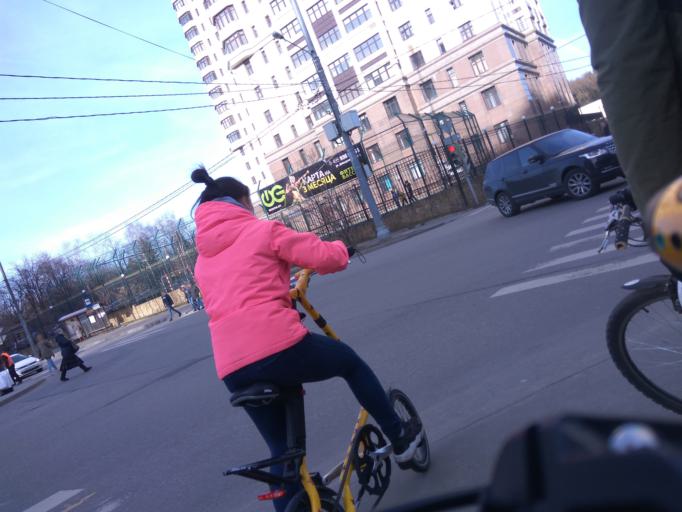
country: RU
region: Moscow
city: Davydkovo
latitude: 55.7270
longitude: 37.4786
